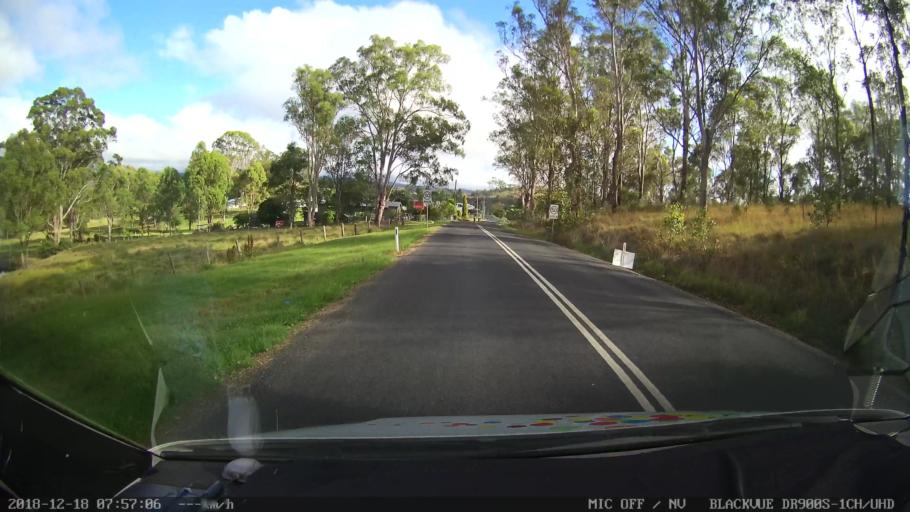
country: AU
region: New South Wales
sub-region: Kyogle
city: Kyogle
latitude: -28.3956
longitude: 152.6108
